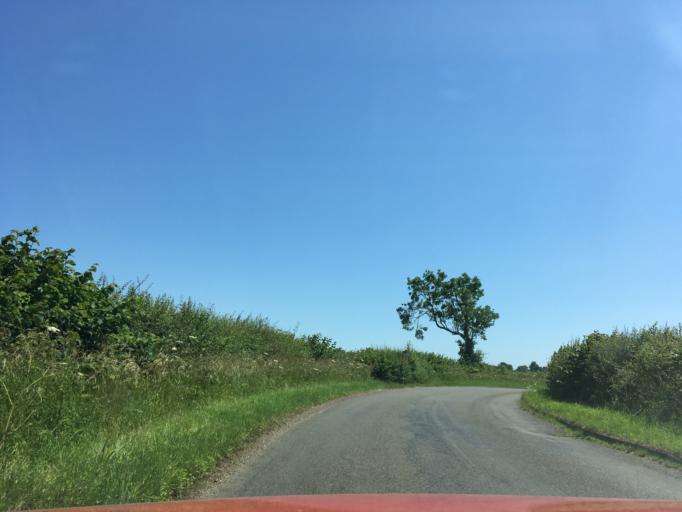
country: GB
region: England
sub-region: Milton Keynes
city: Calverton
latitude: 52.0045
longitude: -0.8438
